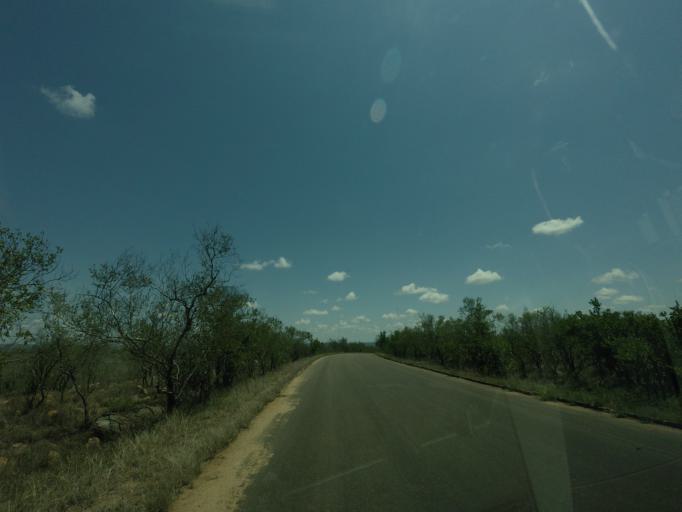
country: ZA
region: Mpumalanga
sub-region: Ehlanzeni District
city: Komatipoort
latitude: -24.8476
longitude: 31.8939
